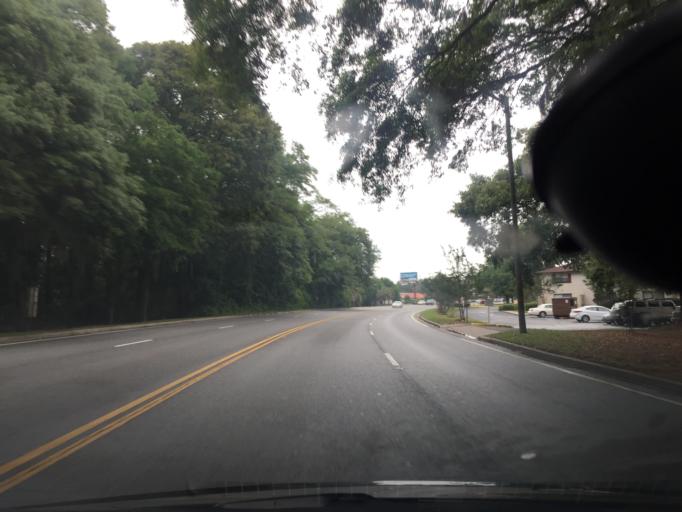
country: US
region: Georgia
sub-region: Chatham County
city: Isle of Hope
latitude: 31.9914
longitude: -81.1059
